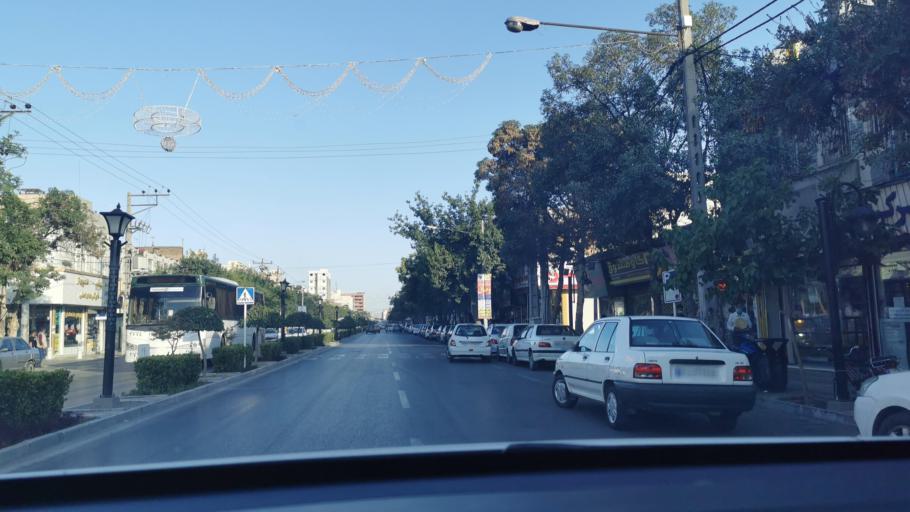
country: IR
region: Razavi Khorasan
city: Mashhad
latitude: 36.2970
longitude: 59.6425
